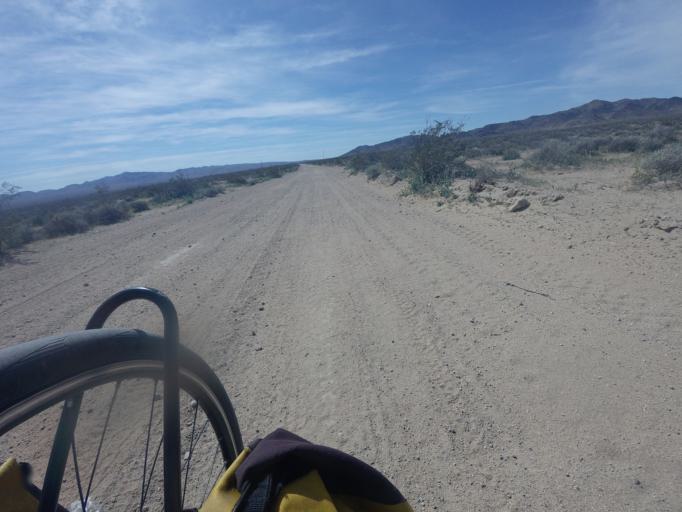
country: US
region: California
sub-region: San Bernardino County
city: Searles Valley
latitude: 35.5724
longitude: -117.4396
